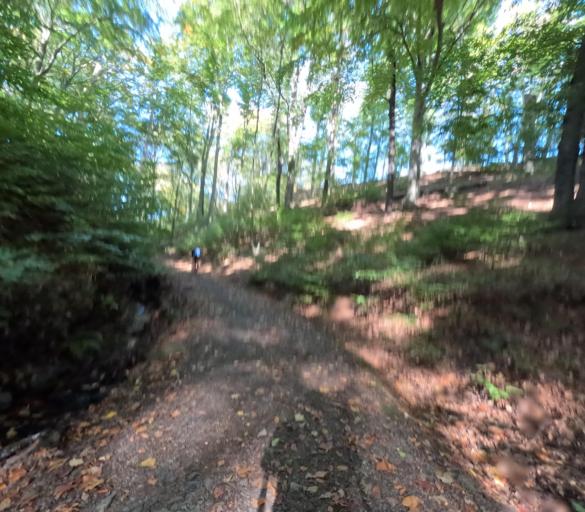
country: DE
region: Saxony
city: Radebeul
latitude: 51.1164
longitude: 13.6942
